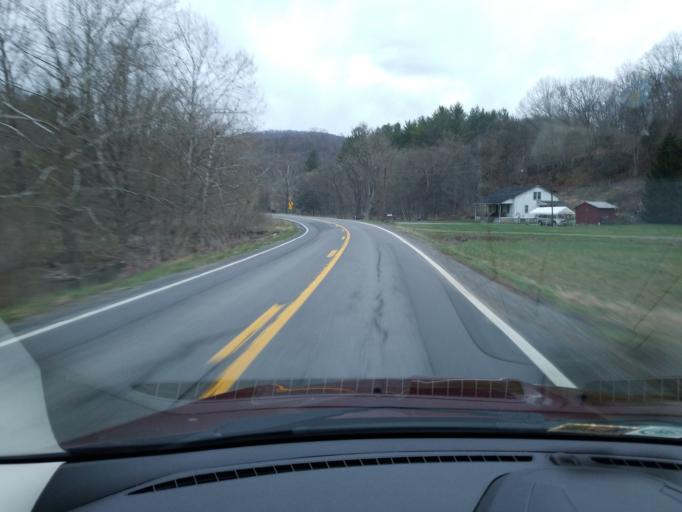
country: US
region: West Virginia
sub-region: Monroe County
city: Union
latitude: 37.5721
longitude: -80.5651
